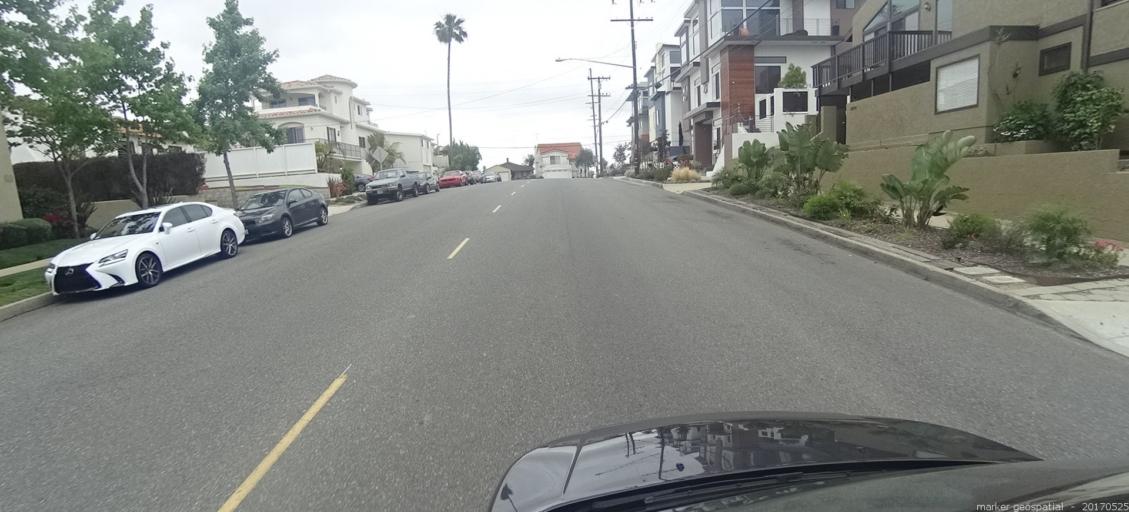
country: US
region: California
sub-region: Los Angeles County
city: Redondo Beach
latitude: 33.8406
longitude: -118.3774
